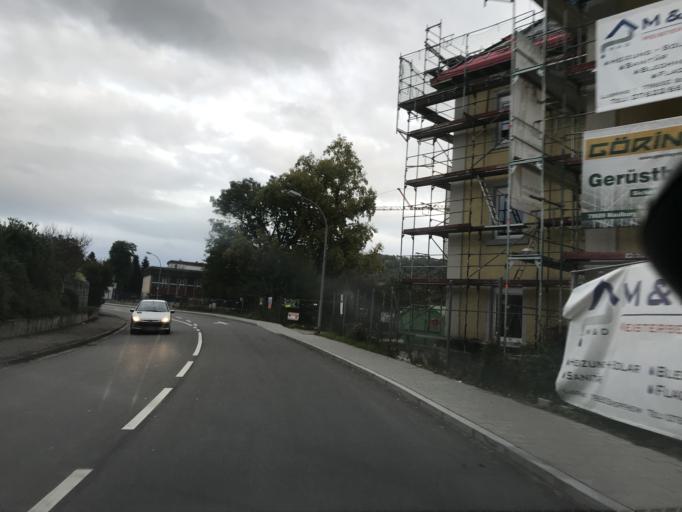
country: DE
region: Baden-Wuerttemberg
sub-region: Freiburg Region
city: Steinen
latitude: 47.6417
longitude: 7.7346
